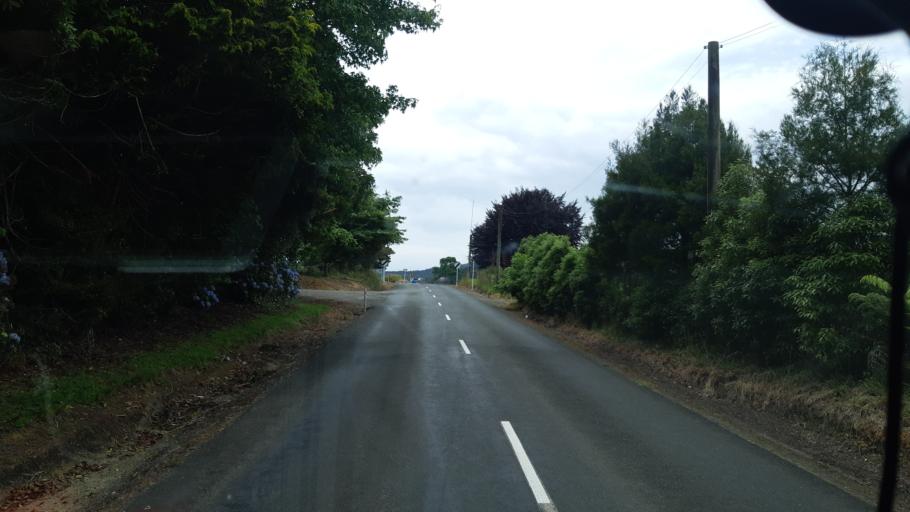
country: NZ
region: Waikato
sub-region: Waikato District
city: Raglan
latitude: -37.8393
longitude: 175.0247
